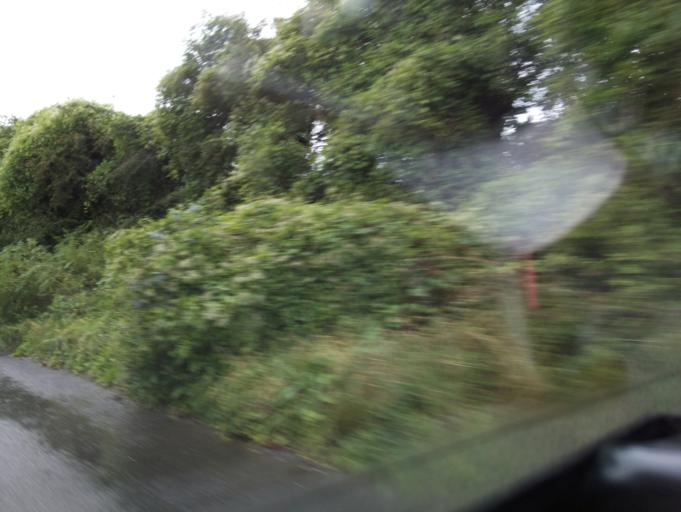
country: GB
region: England
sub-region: Devon
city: South Brent
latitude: 50.4189
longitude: -3.8370
